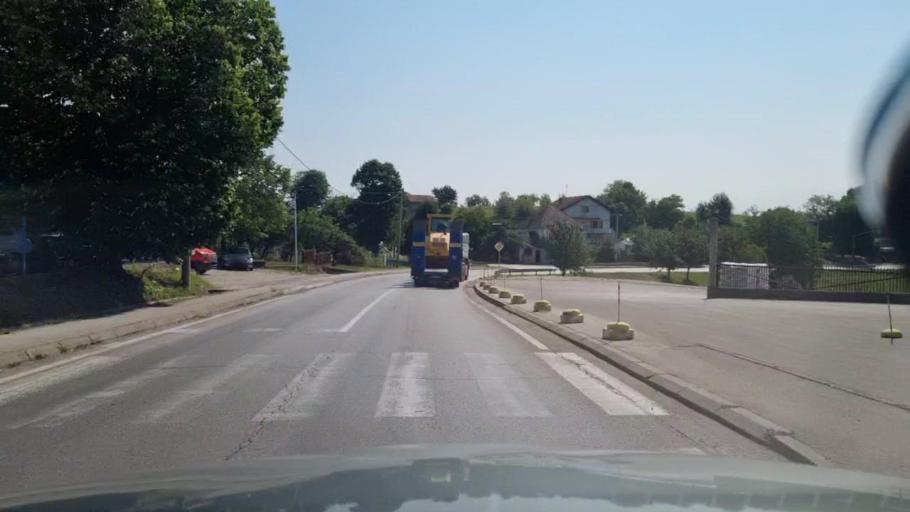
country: BA
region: Federation of Bosnia and Herzegovina
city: Mionica
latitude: 44.8422
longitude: 18.4487
